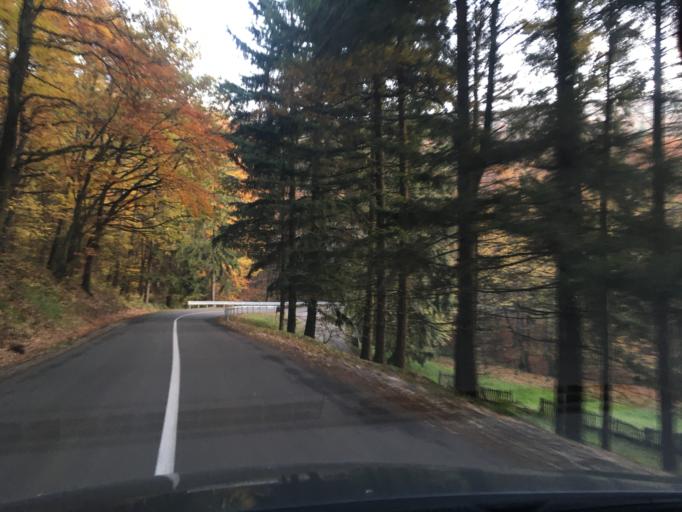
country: RS
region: Central Serbia
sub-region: Belgrade
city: Sopot
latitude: 44.4726
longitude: 20.5724
